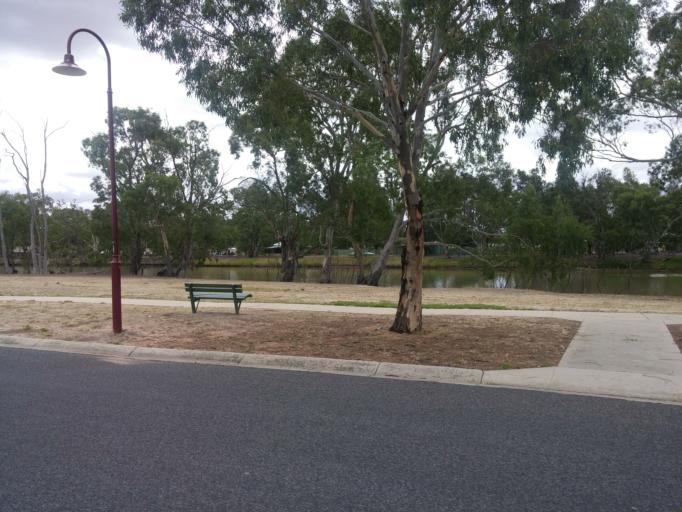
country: AU
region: Victoria
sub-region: Horsham
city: Horsham
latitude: -36.7243
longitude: 142.2008
